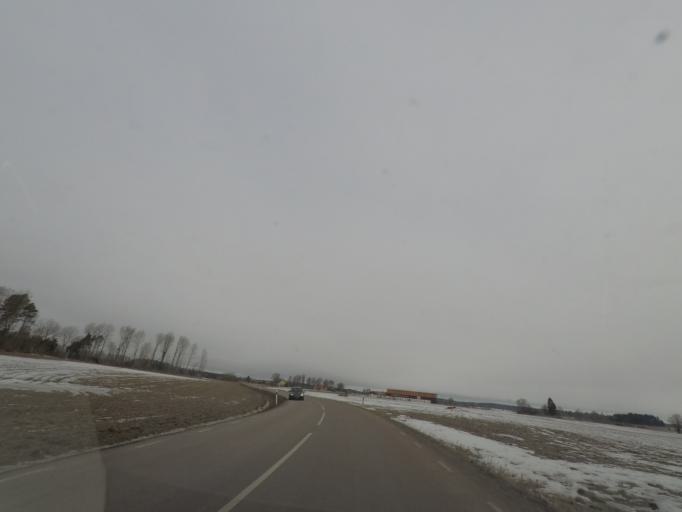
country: SE
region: Vaestmanland
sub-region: Vasteras
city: Skultuna
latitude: 59.7249
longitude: 16.4219
